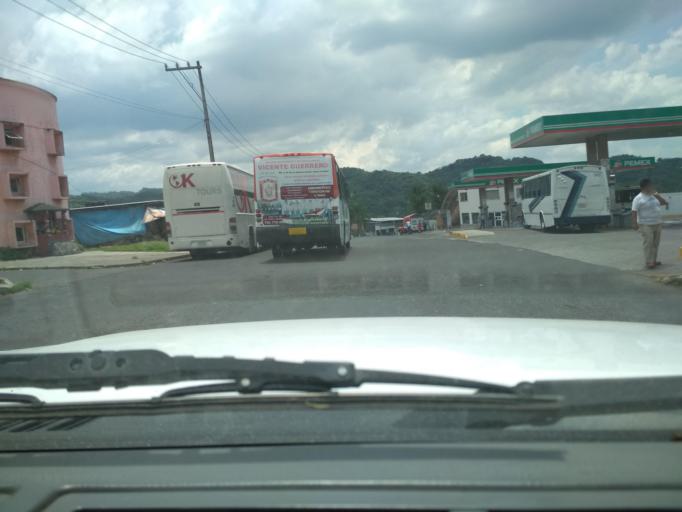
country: MX
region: Veracruz
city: Cordoba
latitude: 18.8847
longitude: -96.9212
